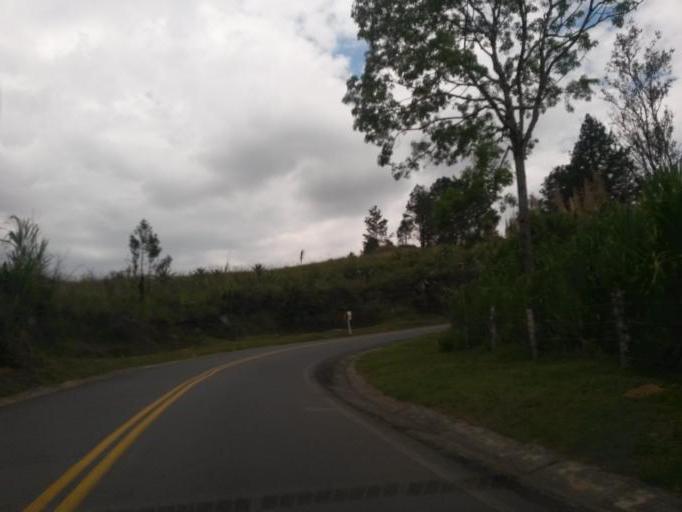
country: CO
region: Cauca
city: Lopez
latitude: 2.4740
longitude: -76.7259
